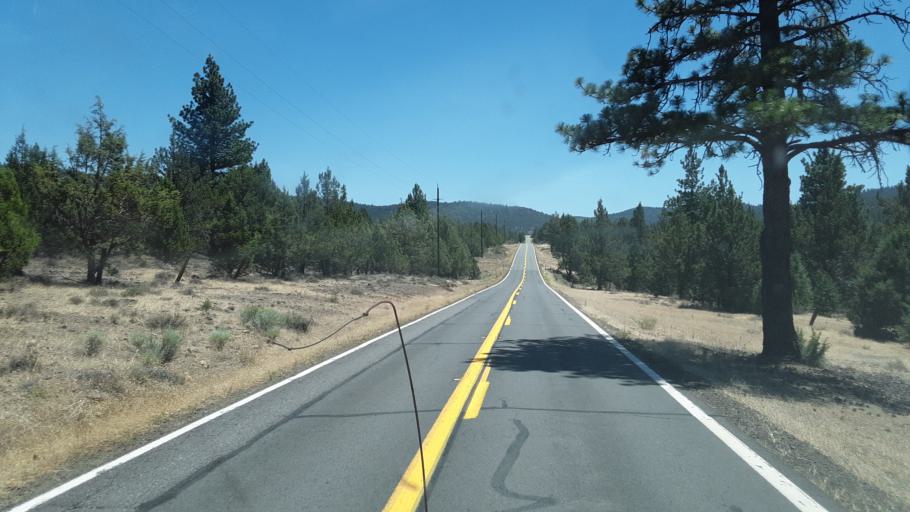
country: US
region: California
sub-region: Modoc County
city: Alturas
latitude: 41.0613
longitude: -120.8783
